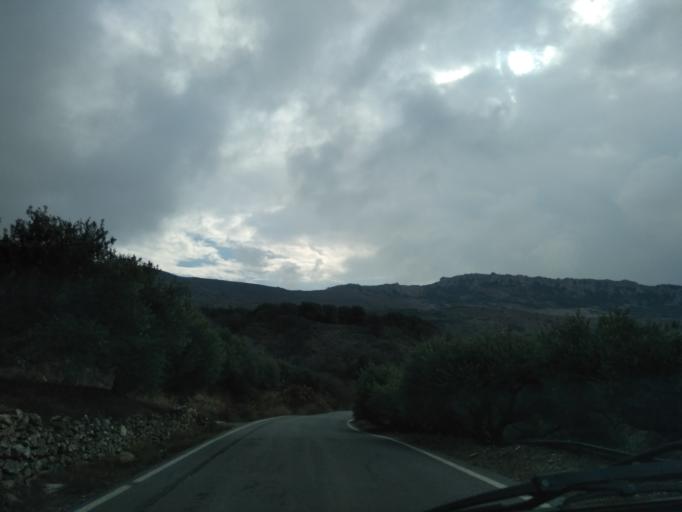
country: GR
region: Crete
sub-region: Nomos Lasithiou
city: Siteia
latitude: 35.1383
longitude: 26.0226
